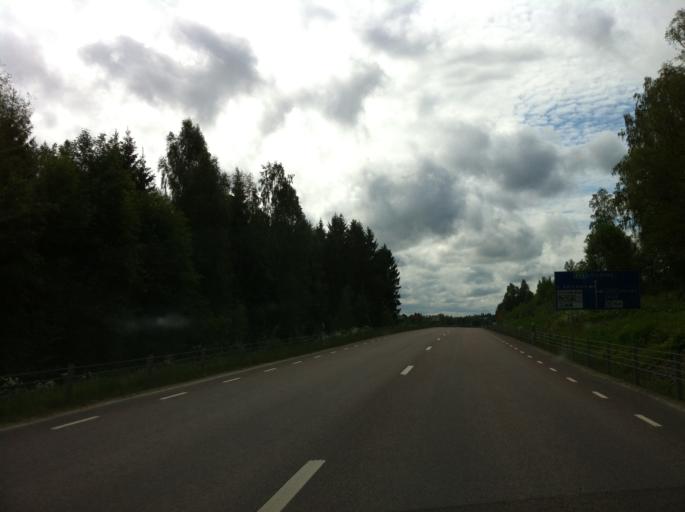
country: SE
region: Vaermland
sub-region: Sunne Kommun
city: Sunne
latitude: 59.7419
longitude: 13.1286
